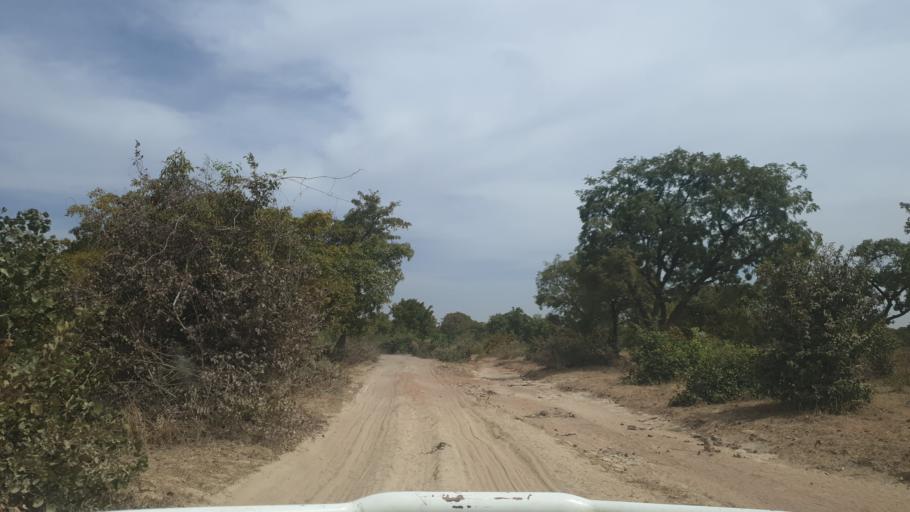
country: ML
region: Sikasso
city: Yorosso
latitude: 12.2411
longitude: -4.7336
